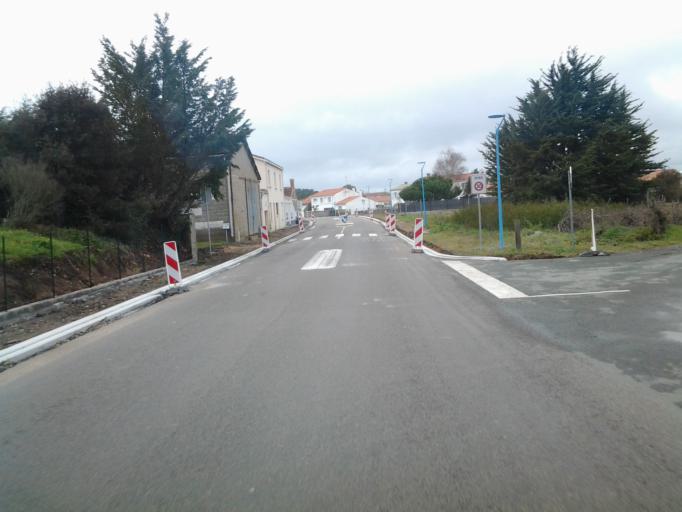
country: FR
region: Pays de la Loire
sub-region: Departement de la Vendee
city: Longeville-sur-Mer
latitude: 46.3847
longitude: -1.4662
